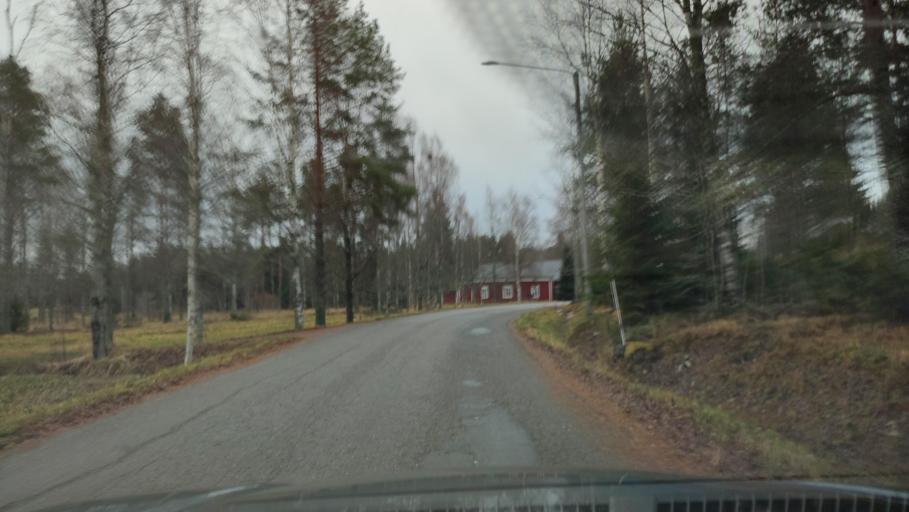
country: FI
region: Southern Ostrobothnia
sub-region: Suupohja
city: Karijoki
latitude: 62.1366
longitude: 21.5730
